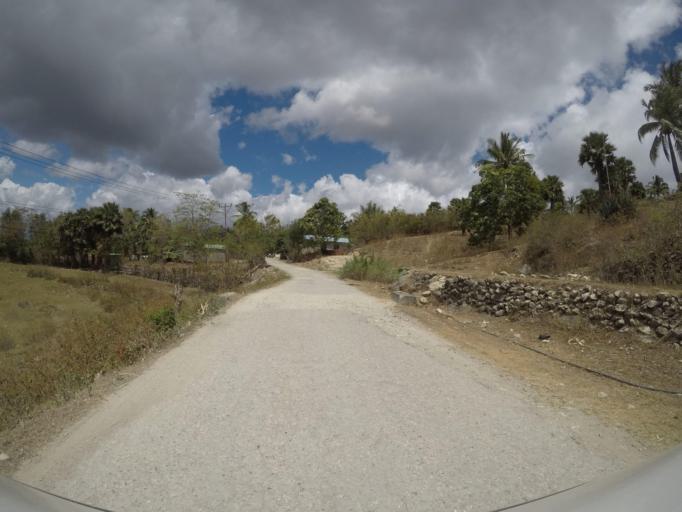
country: TL
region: Baucau
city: Baucau
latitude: -8.5180
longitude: 126.6906
